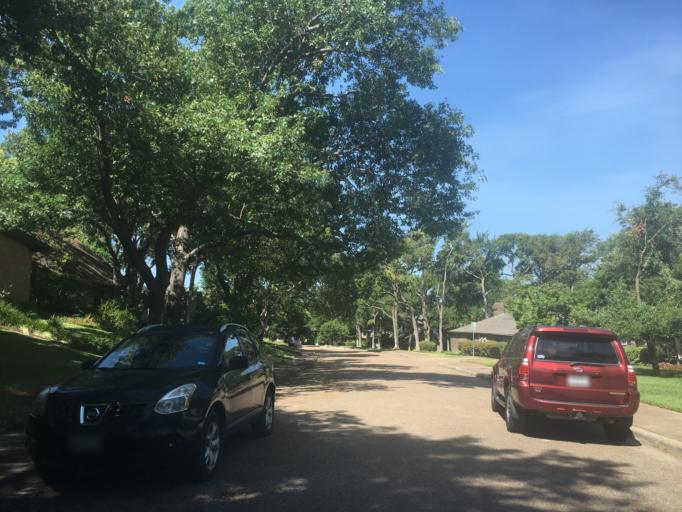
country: US
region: Texas
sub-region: Dallas County
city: Richardson
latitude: 32.8748
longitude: -96.7187
